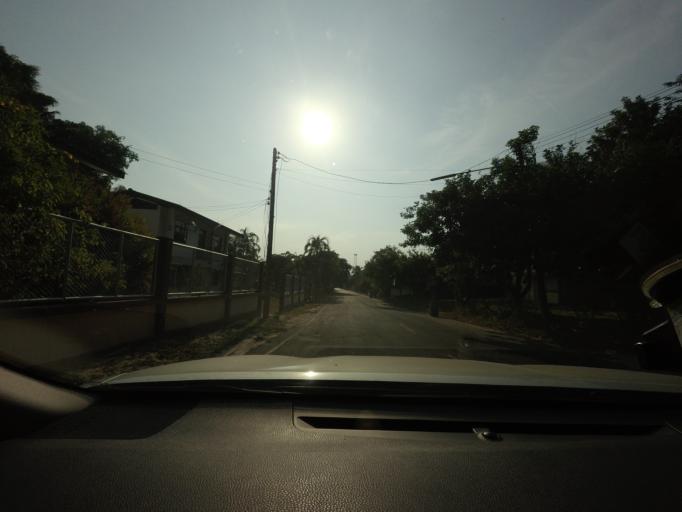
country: TH
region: Narathiwat
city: Rueso
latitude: 6.4002
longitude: 101.5250
